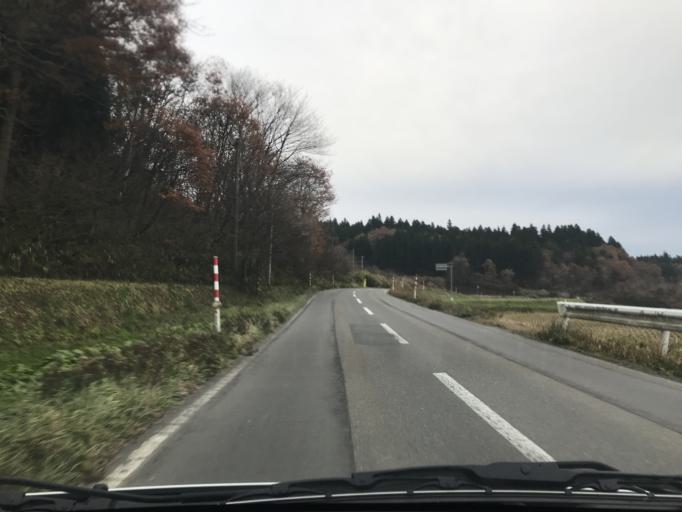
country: JP
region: Iwate
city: Kitakami
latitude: 39.2637
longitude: 141.2685
